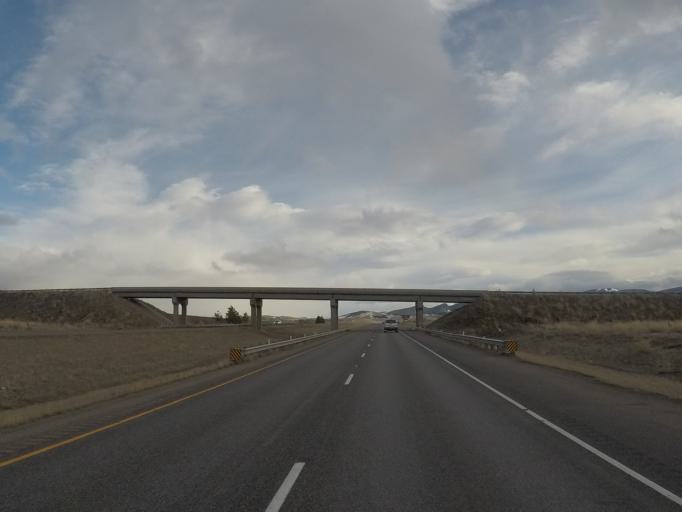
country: US
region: Montana
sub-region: Deer Lodge County
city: Warm Springs
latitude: 46.1084
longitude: -112.7973
